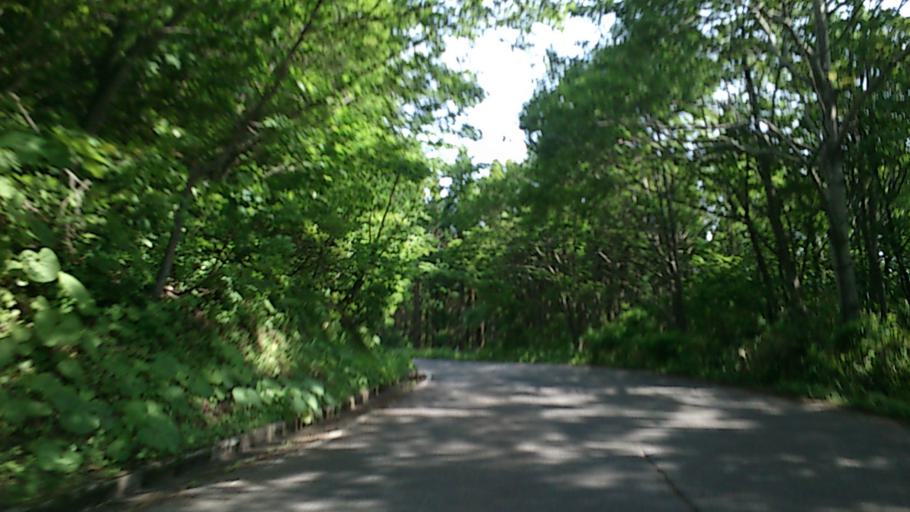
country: JP
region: Aomori
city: Aomori Shi
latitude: 40.7194
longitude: 140.8090
